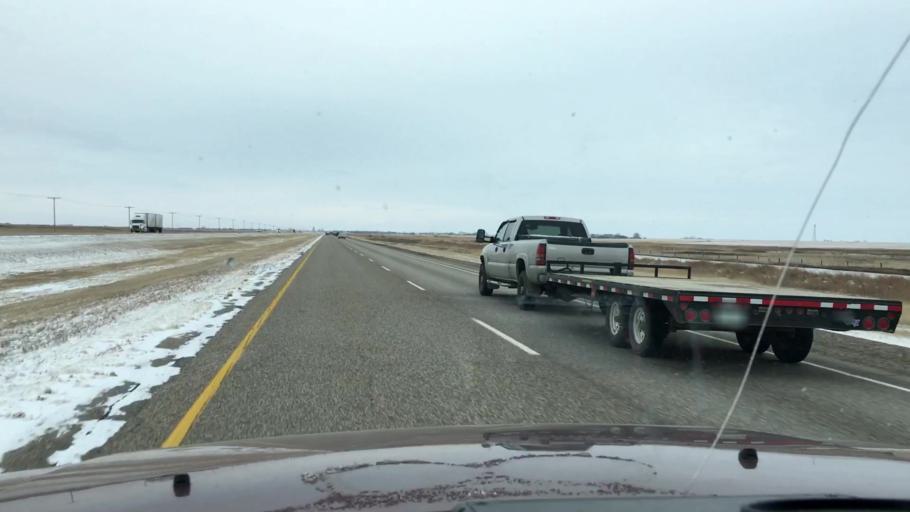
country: CA
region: Saskatchewan
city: Watrous
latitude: 51.0915
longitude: -105.8588
